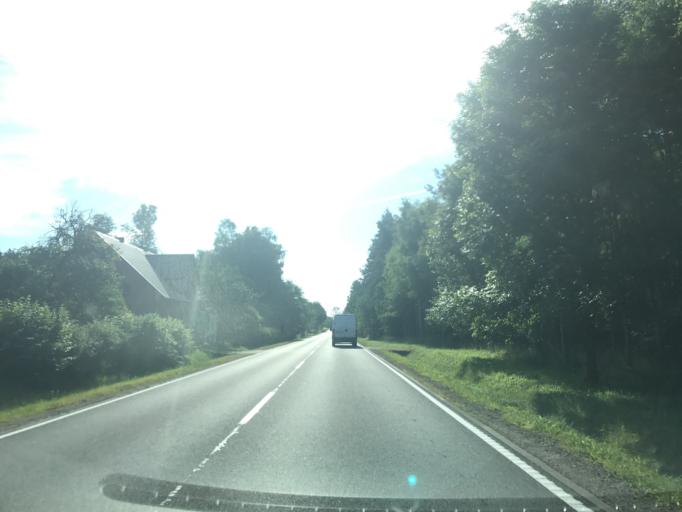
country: PL
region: Pomeranian Voivodeship
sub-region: Powiat czluchowski
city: Rzeczenica
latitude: 53.7507
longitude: 17.1497
